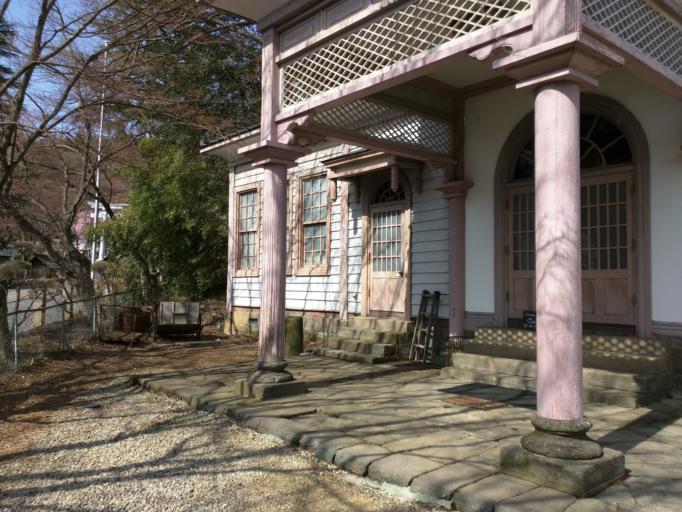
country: JP
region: Tochigi
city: Kuroiso
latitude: 37.1115
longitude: 140.2189
